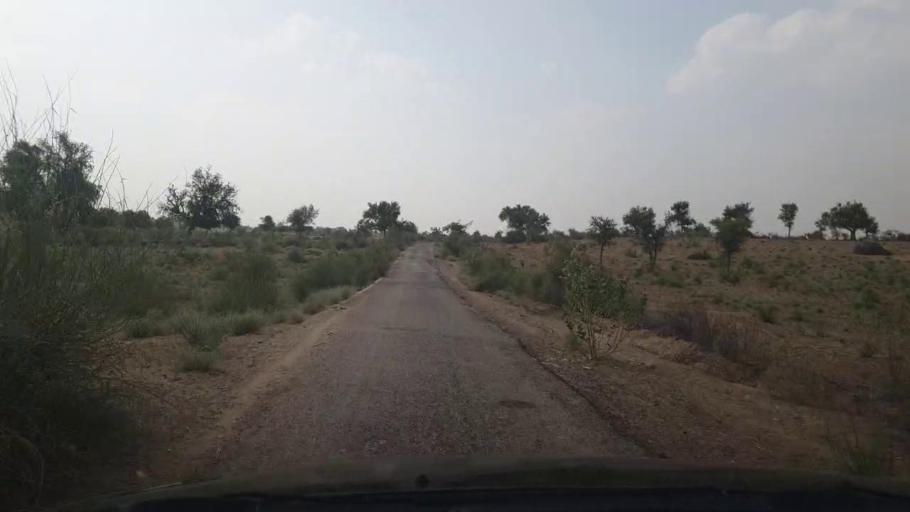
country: PK
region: Sindh
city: Islamkot
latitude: 24.9718
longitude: 70.5897
